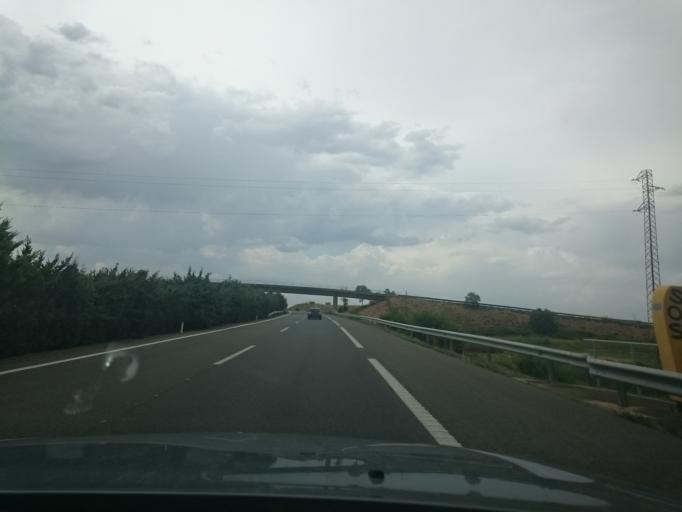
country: ES
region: Navarre
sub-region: Provincia de Navarra
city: Fontellas
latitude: 42.0078
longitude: -1.5892
